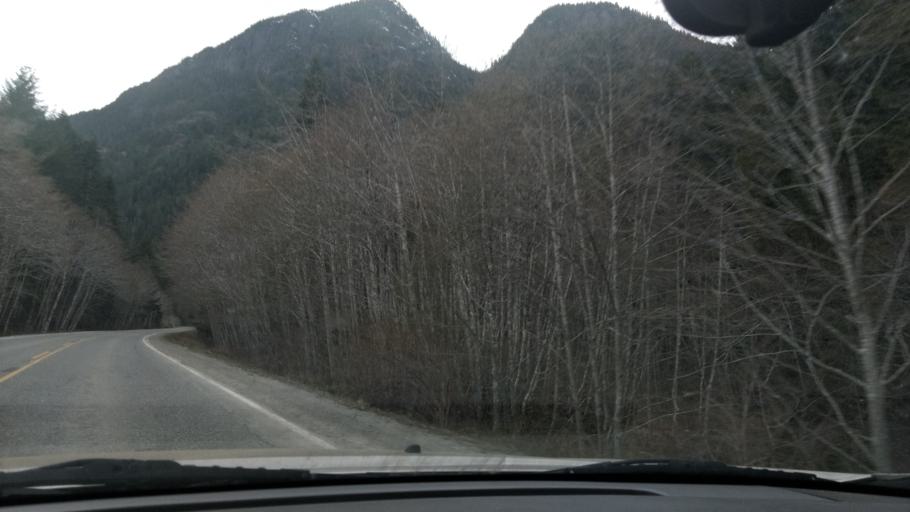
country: CA
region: British Columbia
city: Campbell River
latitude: 49.8538
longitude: -125.8314
